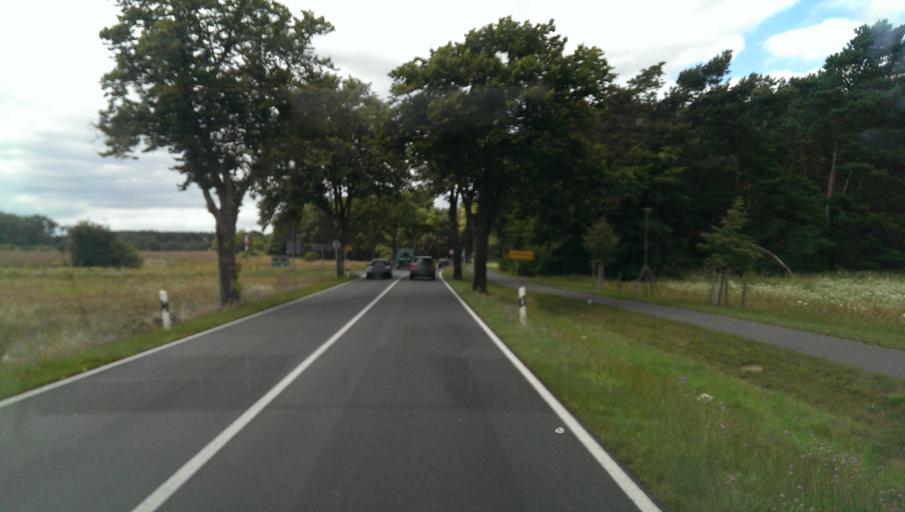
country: DE
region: Brandenburg
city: Belzig
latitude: 52.1281
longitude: 12.6324
